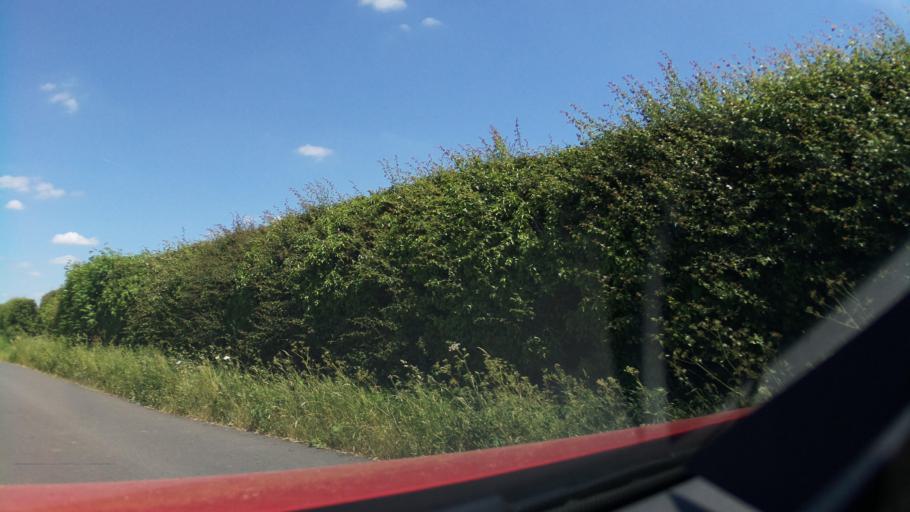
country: GB
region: England
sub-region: Wiltshire
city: Royal Wootton Bassett
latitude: 51.5097
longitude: -1.8995
